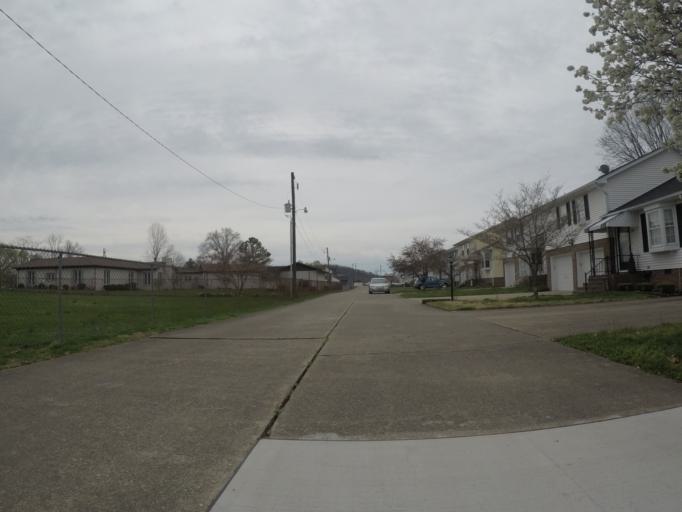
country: US
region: West Virginia
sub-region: Cabell County
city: Barboursville
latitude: 38.4189
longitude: -82.3021
